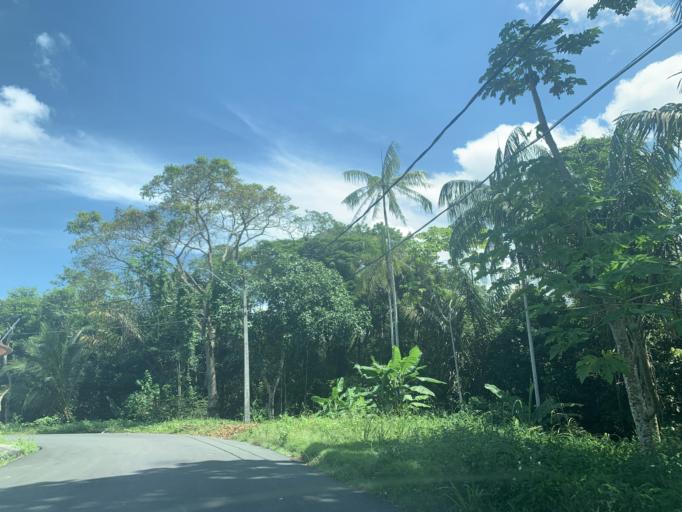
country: BR
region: Amazonas
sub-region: Manaus
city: Manaus
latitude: -3.1020
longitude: -59.9657
